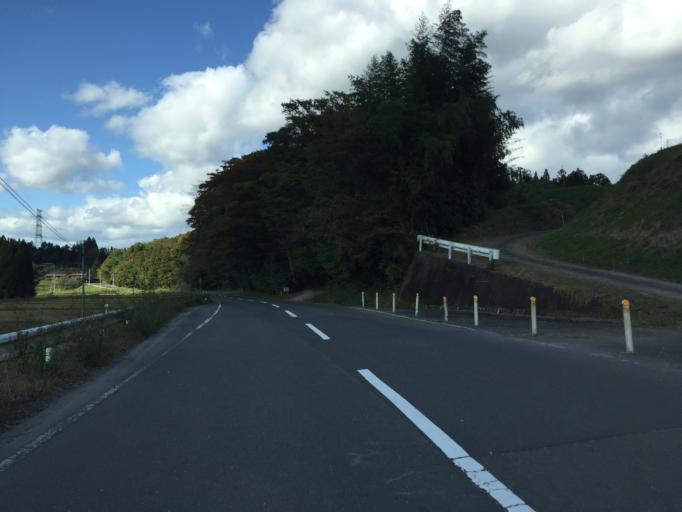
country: JP
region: Miyagi
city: Marumori
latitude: 37.8512
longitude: 140.8322
